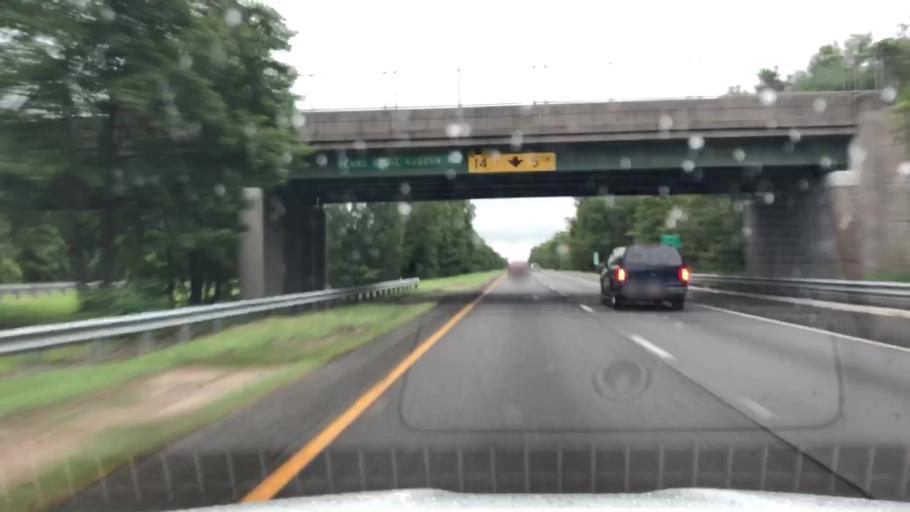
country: US
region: New Jersey
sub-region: Salem County
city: Penns Grove
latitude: 39.7162
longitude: -75.4332
